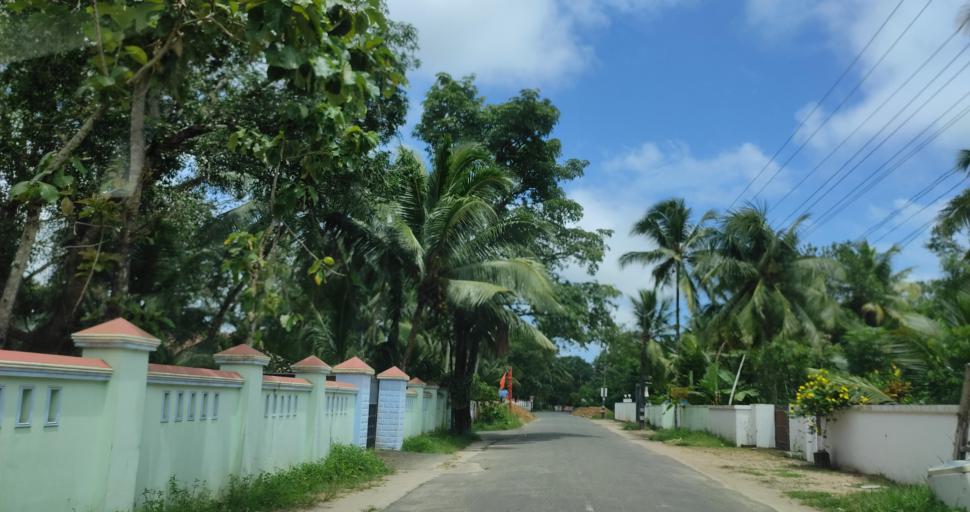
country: IN
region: Kerala
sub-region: Alappuzha
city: Vayalar
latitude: 9.7172
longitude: 76.3375
